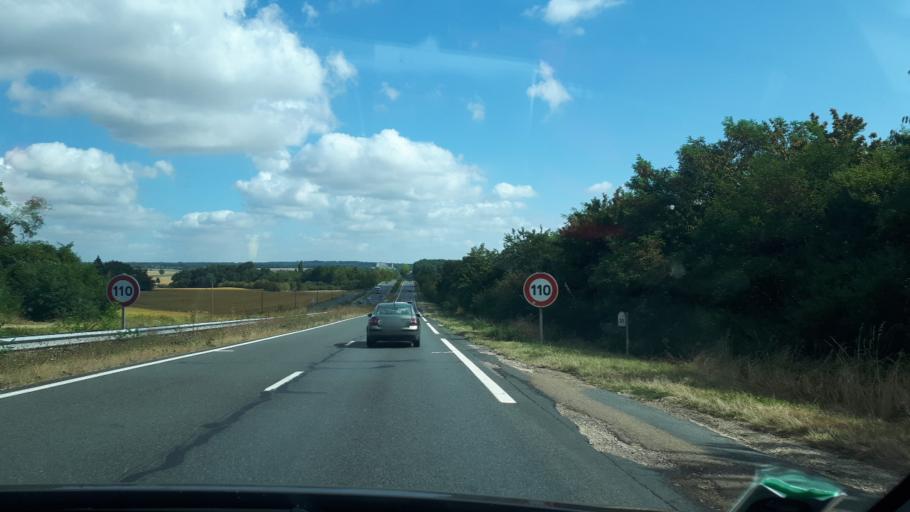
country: FR
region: Centre
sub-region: Departement du Loir-et-Cher
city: Saint-Ouen
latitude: 47.8263
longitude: 1.0783
